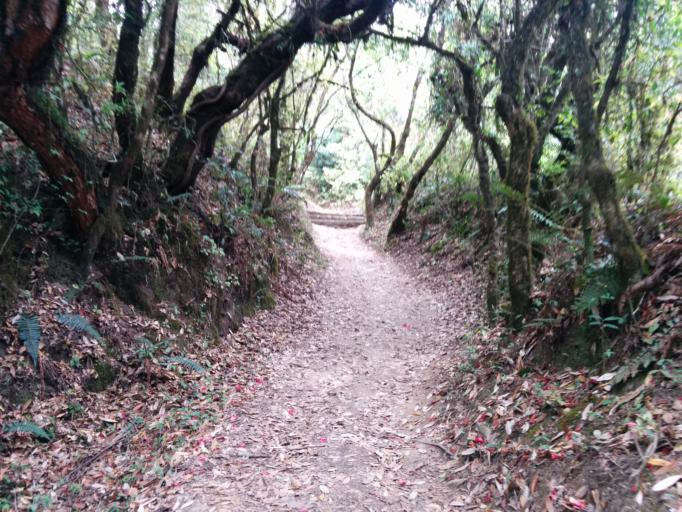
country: NP
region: Central Region
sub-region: Bagmati Zone
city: Nagarkot
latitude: 27.7904
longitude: 85.4366
